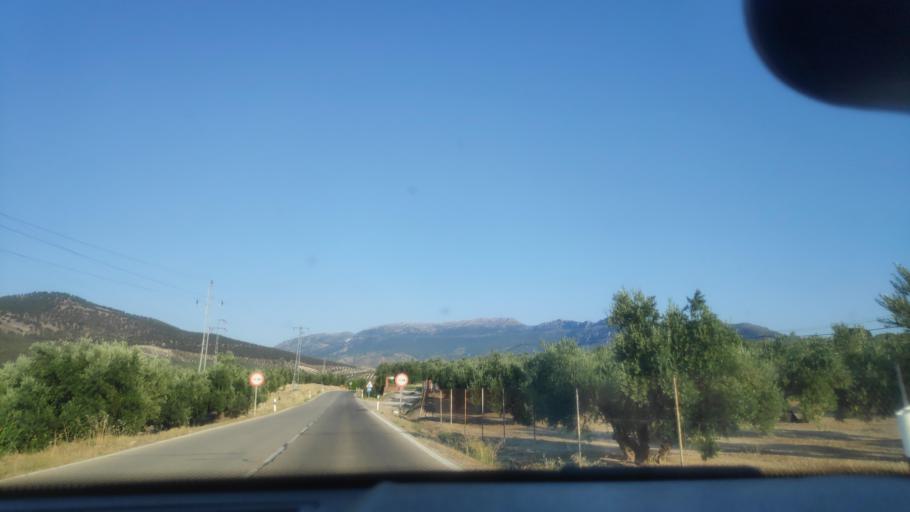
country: ES
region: Andalusia
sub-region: Provincia de Jaen
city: Jaen
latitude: 37.7308
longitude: -3.7653
